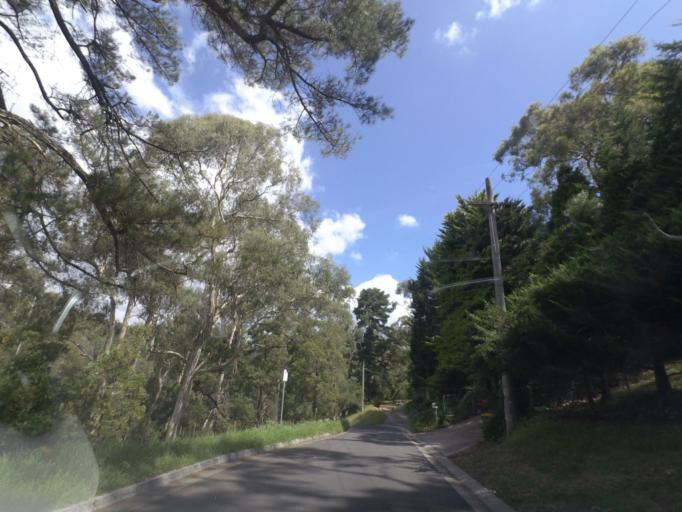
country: AU
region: Victoria
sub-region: Yarra Ranges
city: Mount Evelyn
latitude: -37.7846
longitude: 145.3605
